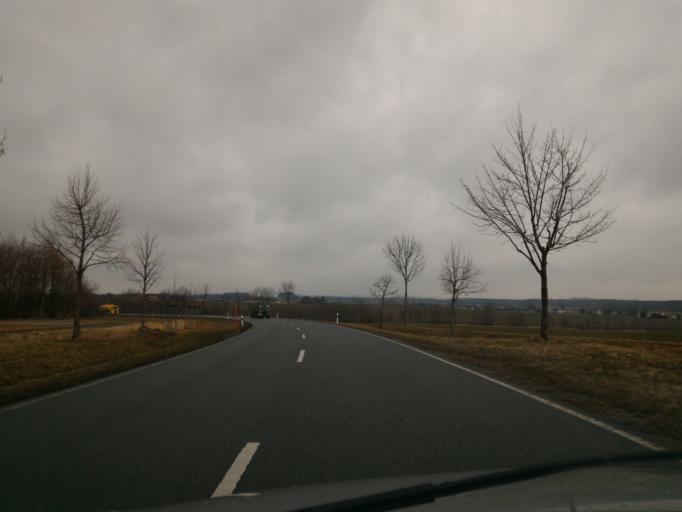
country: DE
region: Saxony
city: Neugersdorf
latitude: 50.9881
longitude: 14.6245
